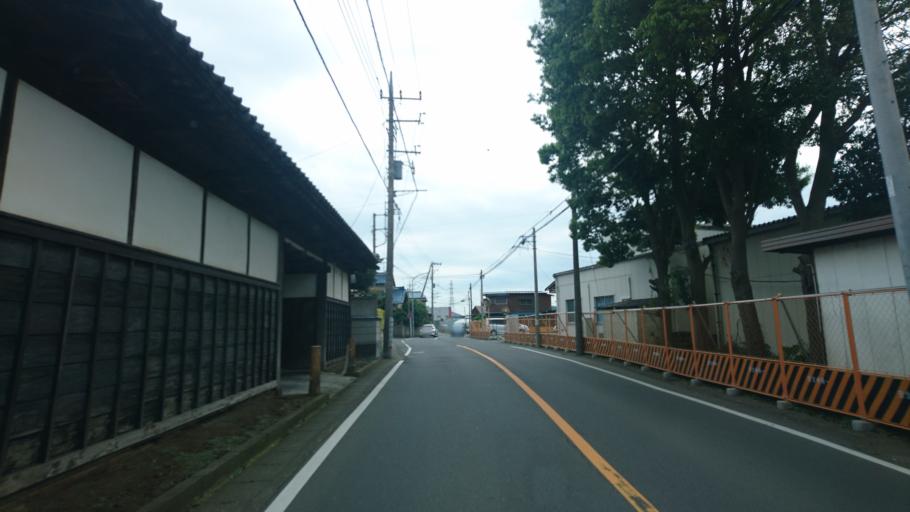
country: JP
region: Kanagawa
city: Fujisawa
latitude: 35.4124
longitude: 139.4786
